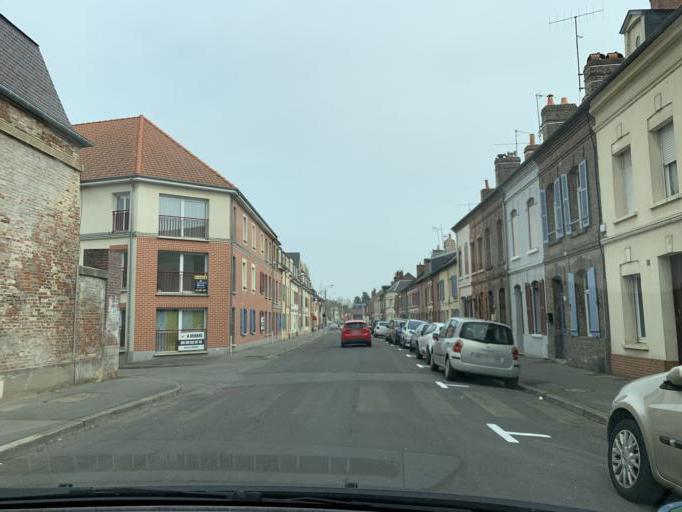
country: FR
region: Picardie
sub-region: Departement de la Somme
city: Abbeville
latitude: 50.1099
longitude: 1.8222
